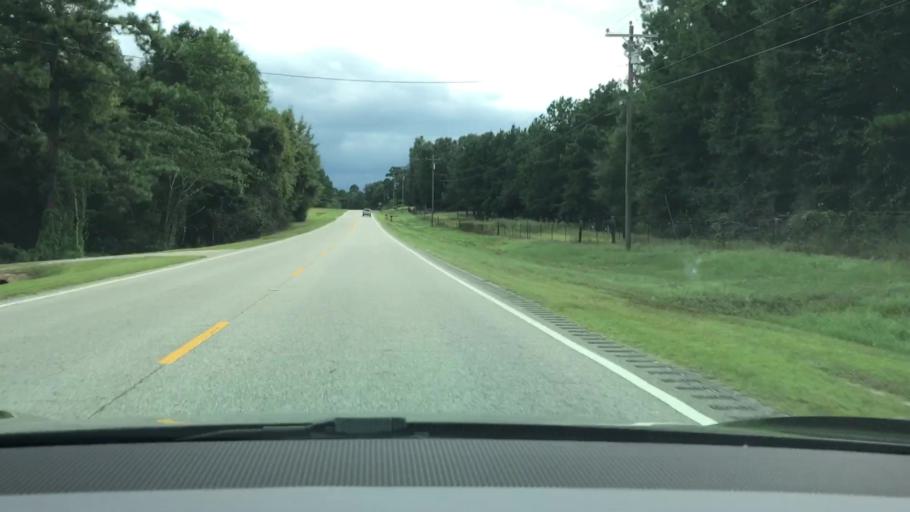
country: US
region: Alabama
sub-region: Coffee County
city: Elba
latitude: 31.5456
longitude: -86.0209
